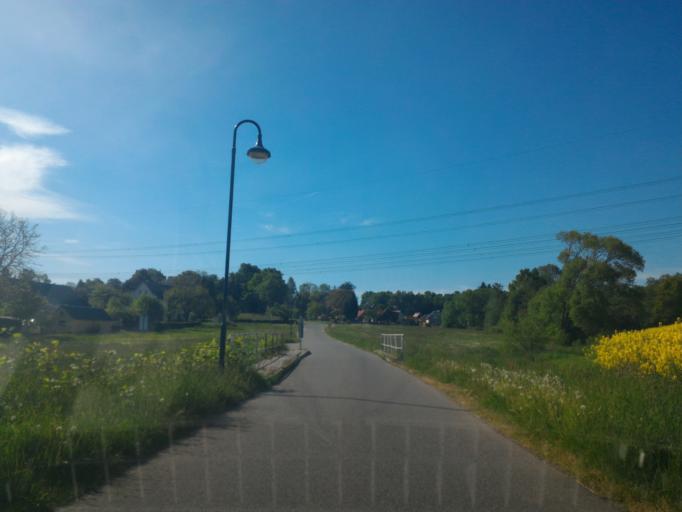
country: DE
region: Saxony
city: Niedercunnersdorf
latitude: 51.0422
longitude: 14.6646
